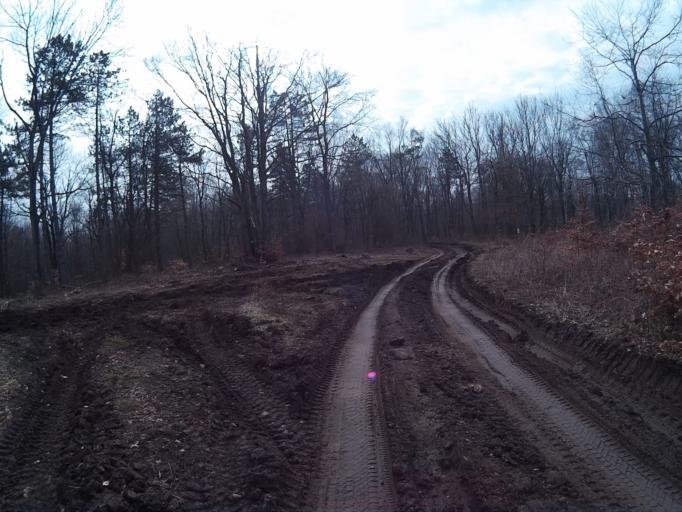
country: HU
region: Veszprem
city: Zirc
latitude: 47.1860
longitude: 17.8360
